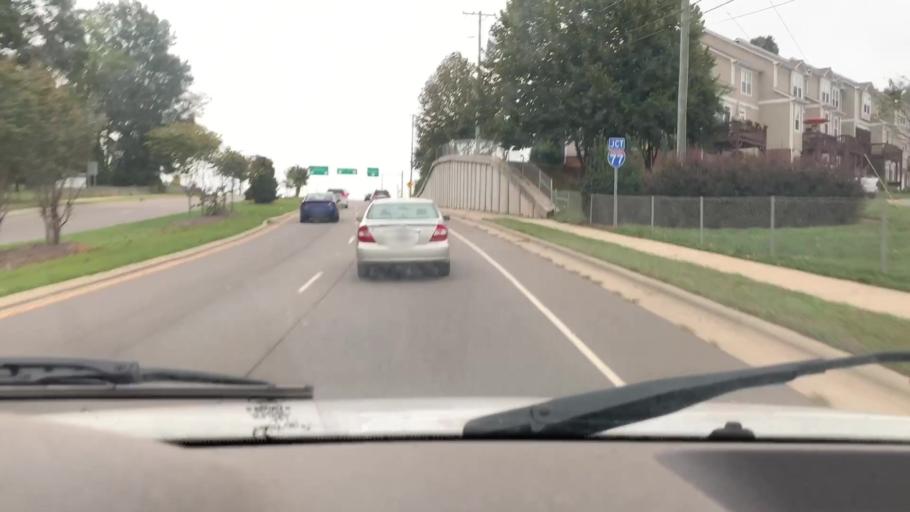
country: US
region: North Carolina
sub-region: Iredell County
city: Mooresville
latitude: 35.5797
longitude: -80.8596
